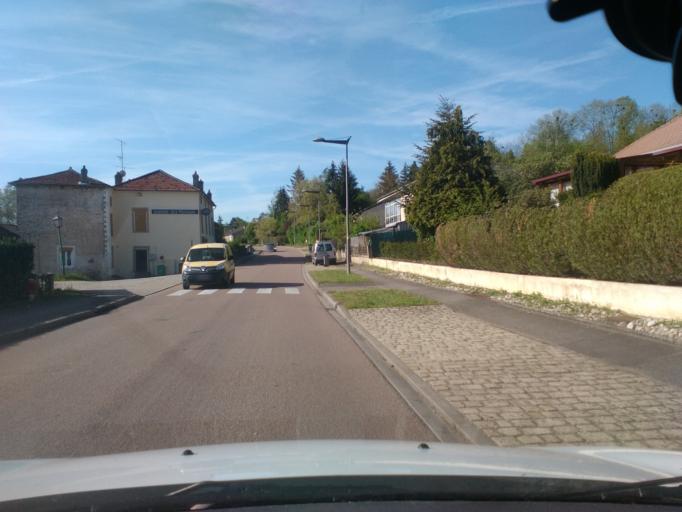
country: FR
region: Lorraine
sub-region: Departement des Vosges
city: Mirecourt
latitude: 48.3187
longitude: 6.1253
